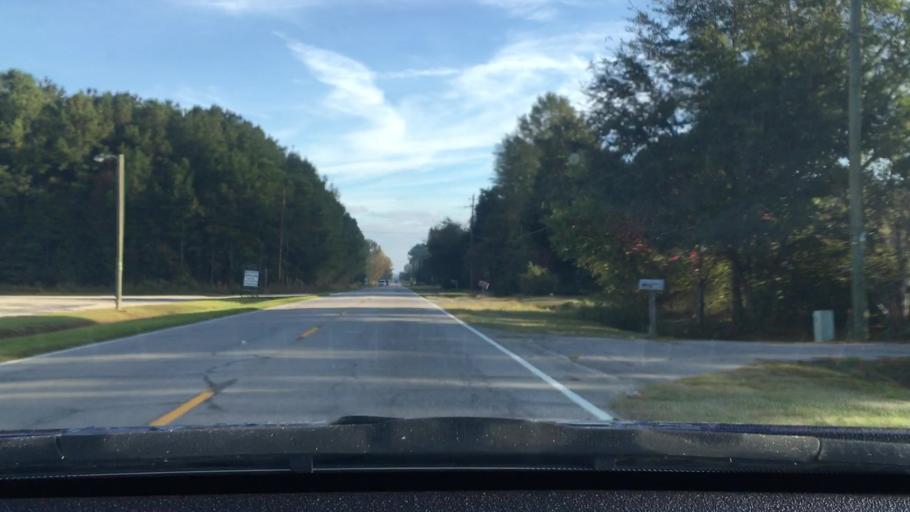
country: US
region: South Carolina
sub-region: Sumter County
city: East Sumter
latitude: 33.9414
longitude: -80.3166
